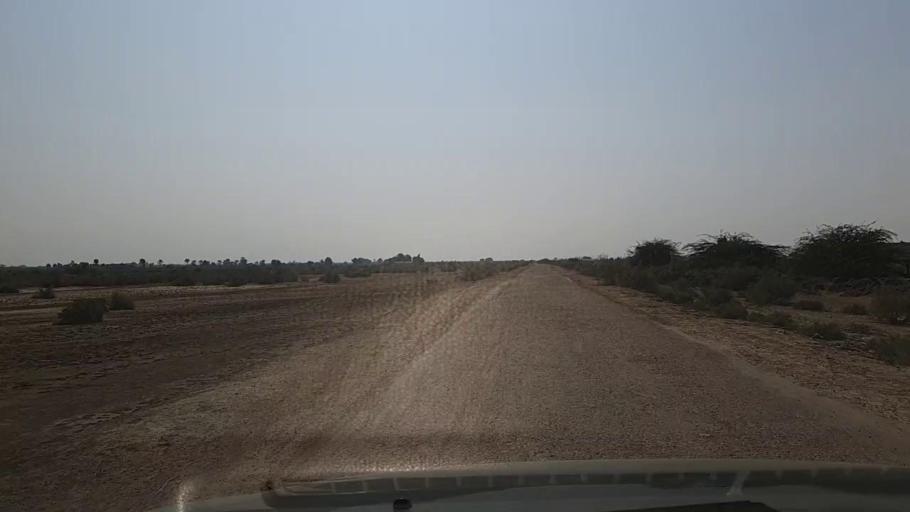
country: PK
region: Sindh
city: Mirpur Sakro
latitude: 24.3861
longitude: 67.6636
